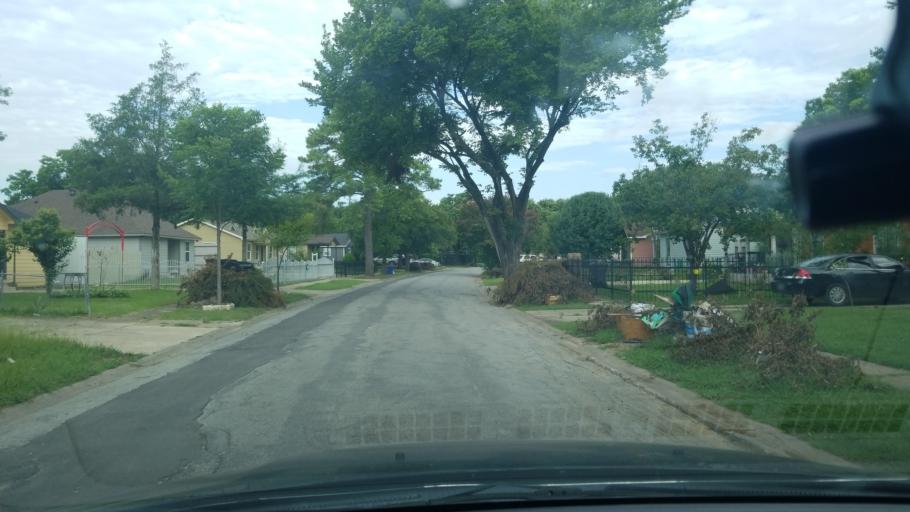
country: US
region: Texas
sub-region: Dallas County
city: Balch Springs
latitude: 32.7351
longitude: -96.6694
